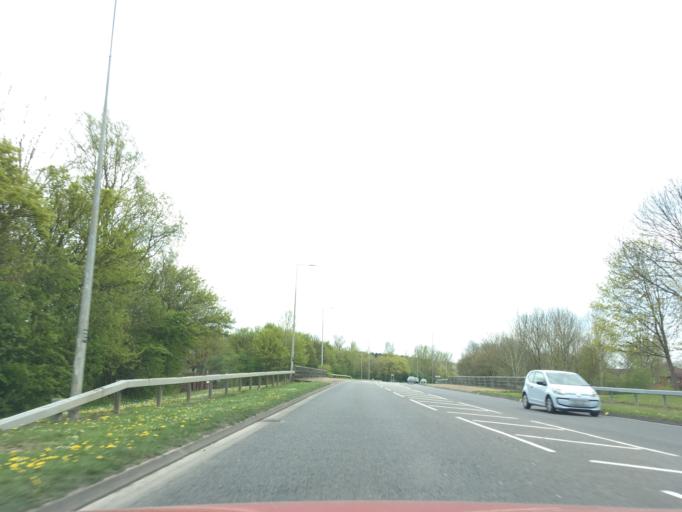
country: GB
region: England
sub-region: Milton Keynes
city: Newport Pagnell
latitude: 52.0613
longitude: -0.7313
